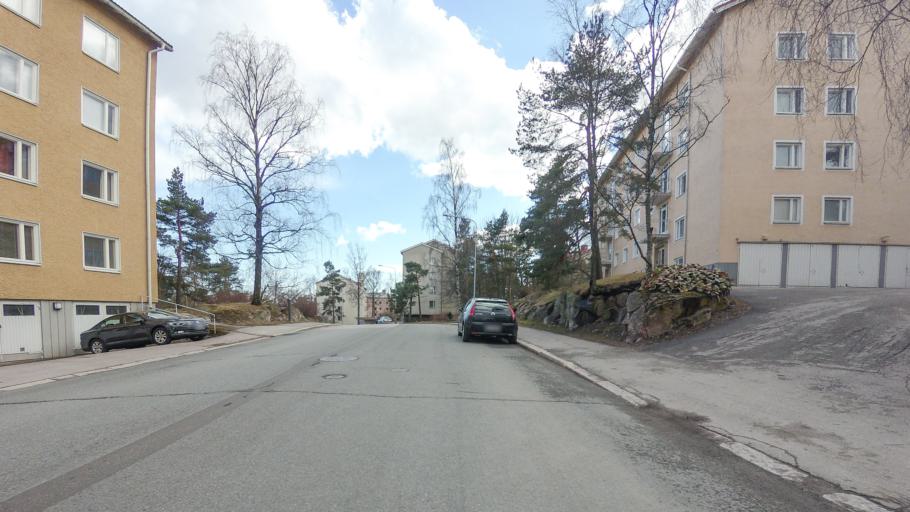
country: FI
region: Uusimaa
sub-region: Helsinki
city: Vantaa
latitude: 60.2011
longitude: 25.0311
